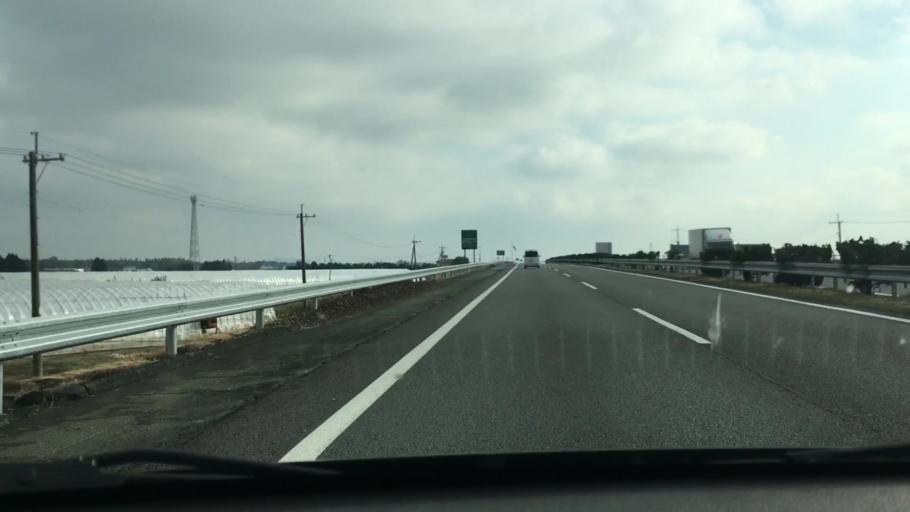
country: JP
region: Kumamoto
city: Ueki
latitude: 32.8905
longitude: 130.7216
